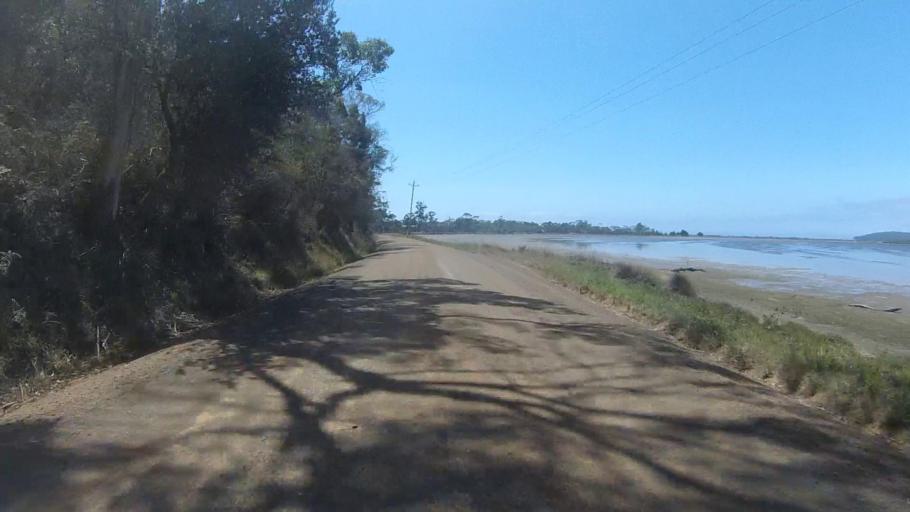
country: AU
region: Tasmania
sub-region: Sorell
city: Sorell
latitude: -42.8490
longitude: 147.8412
